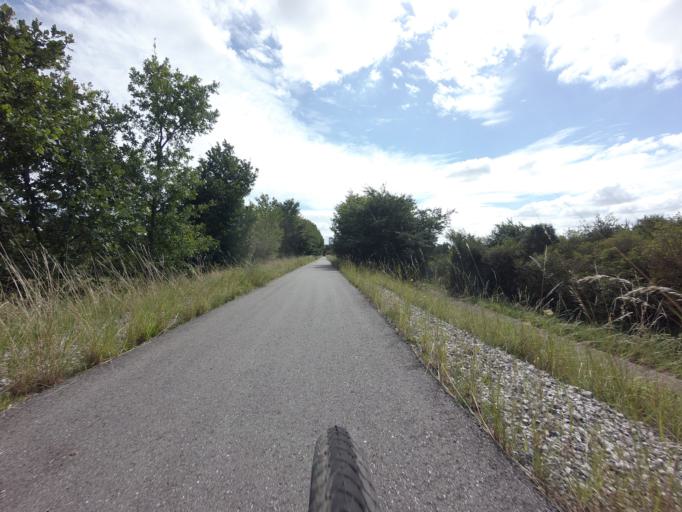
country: DK
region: Central Jutland
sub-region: Norddjurs Kommune
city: Auning
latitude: 56.3940
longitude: 10.4086
